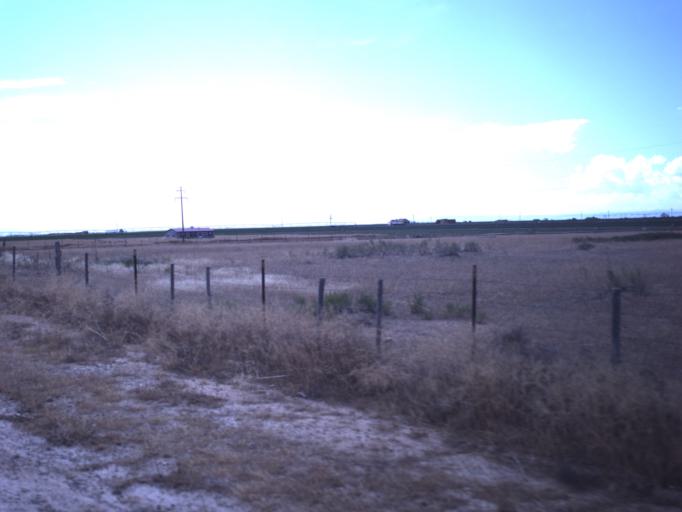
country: US
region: Utah
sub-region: Uintah County
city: Maeser
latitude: 40.2373
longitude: -109.6844
